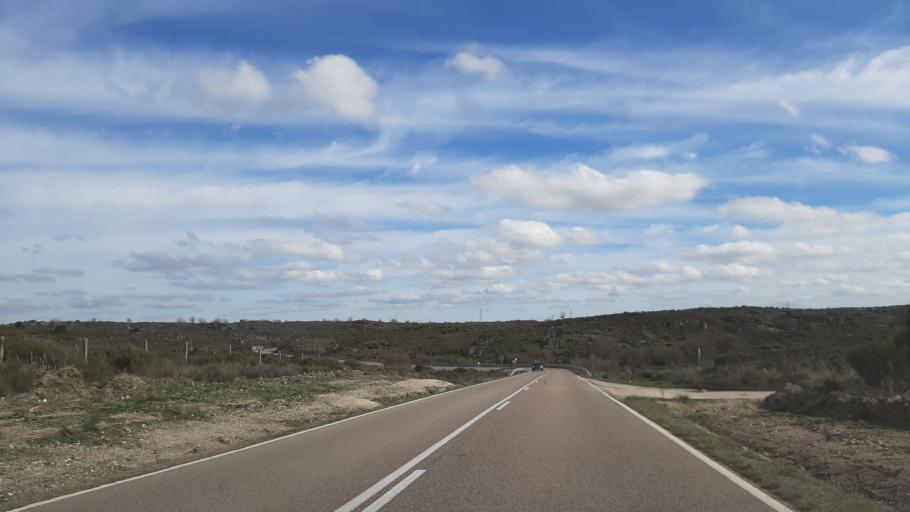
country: ES
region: Castille and Leon
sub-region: Provincia de Salamanca
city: Trabanca
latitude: 41.2574
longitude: -6.4223
